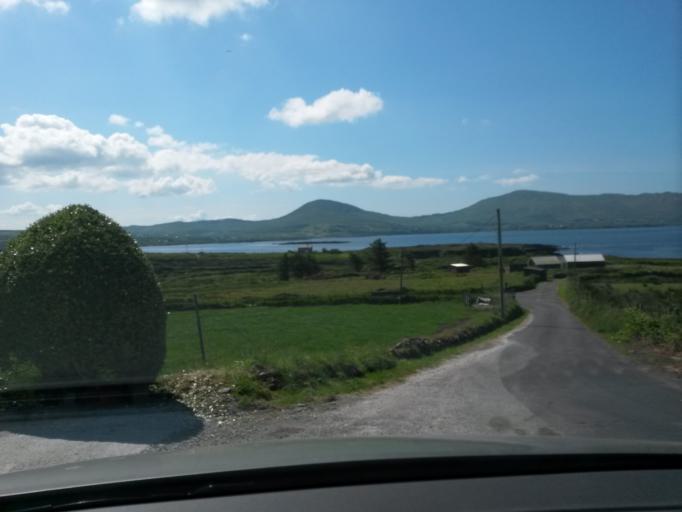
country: IE
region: Munster
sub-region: Ciarrai
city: Cahersiveen
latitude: 51.7180
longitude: -9.9826
